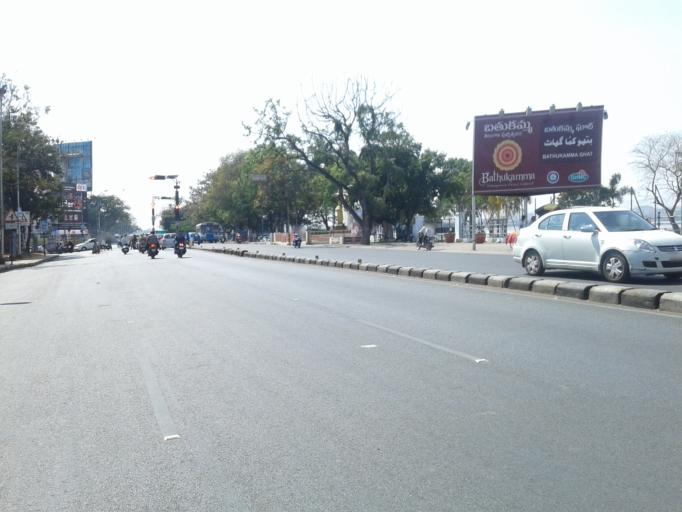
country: IN
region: Telangana
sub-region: Hyderabad
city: Hyderabad
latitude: 17.4221
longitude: 78.4850
